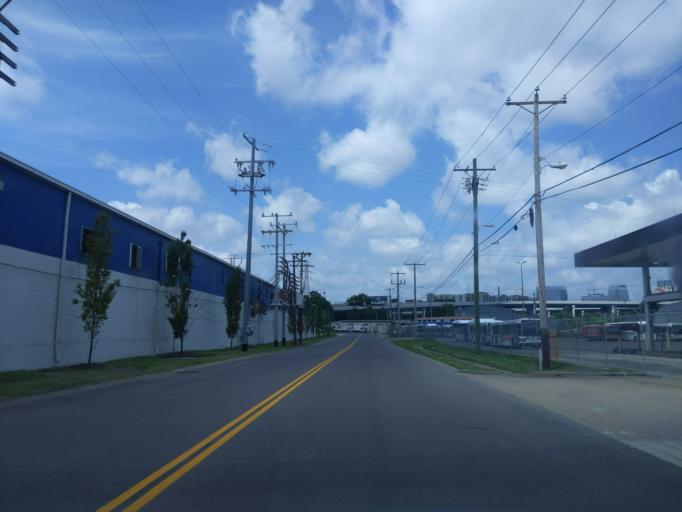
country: US
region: Tennessee
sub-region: Davidson County
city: Nashville
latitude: 36.1566
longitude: -86.7557
